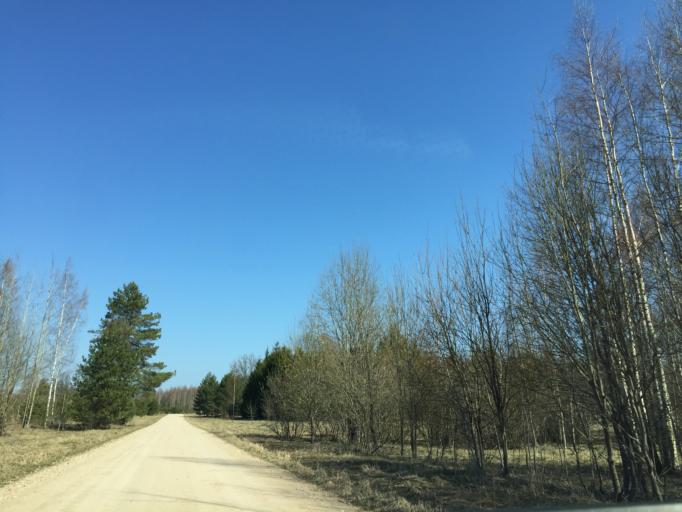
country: EE
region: Tartu
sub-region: Alatskivi vald
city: Kallaste
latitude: 58.5341
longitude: 26.9450
